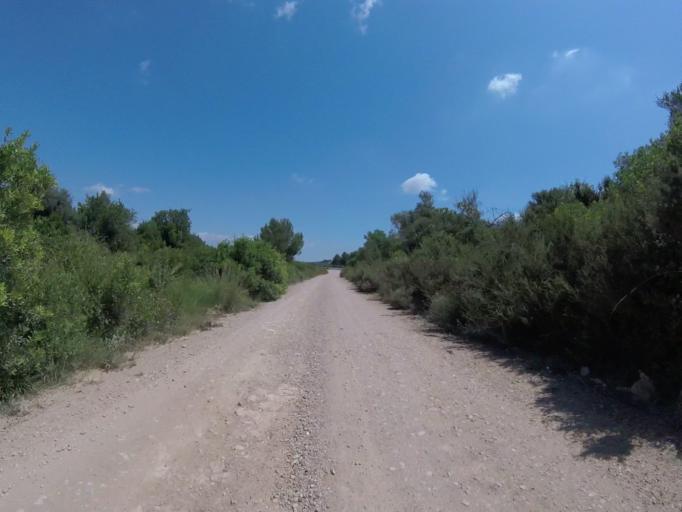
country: ES
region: Valencia
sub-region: Provincia de Castello
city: Torreblanca
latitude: 40.2305
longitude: 0.1598
